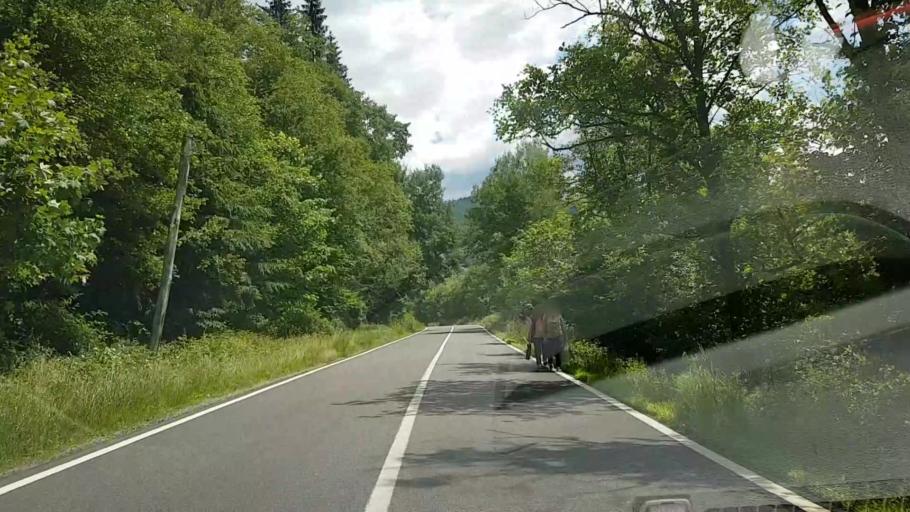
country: RO
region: Suceava
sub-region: Comuna Crucea
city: Crucea
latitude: 47.3939
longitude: 25.5672
